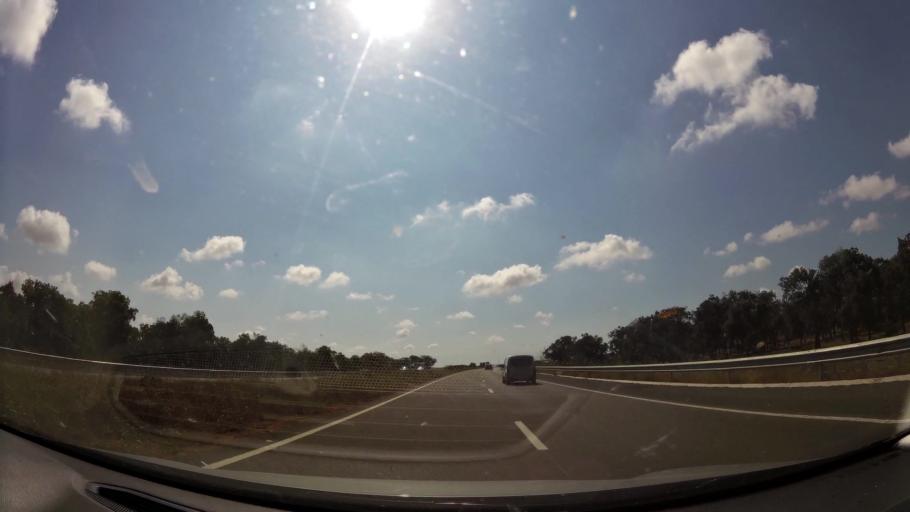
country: MA
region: Rabat-Sale-Zemmour-Zaer
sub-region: Skhirate-Temara
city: Temara
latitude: 33.8382
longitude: -6.8775
